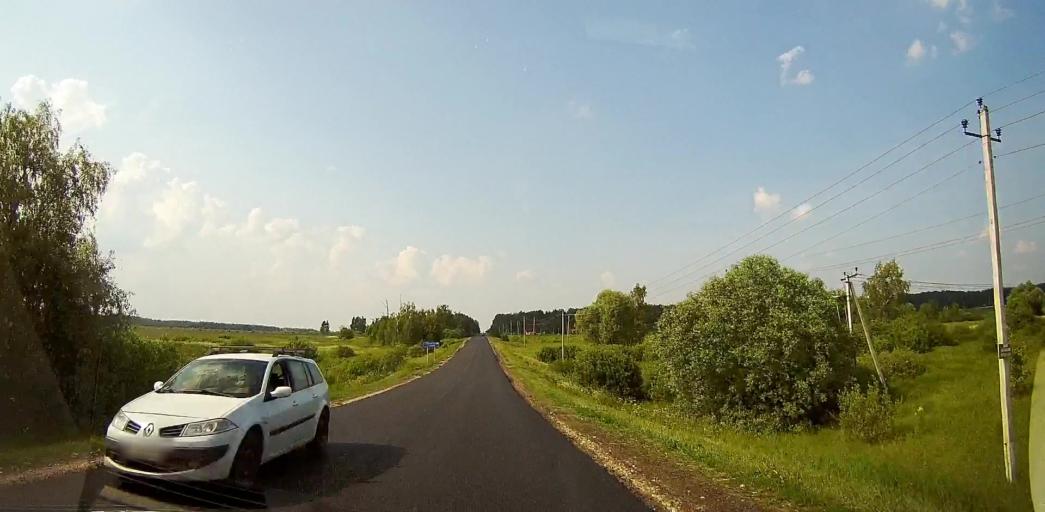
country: RU
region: Moskovskaya
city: Il'inskoye
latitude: 55.2278
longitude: 37.9243
